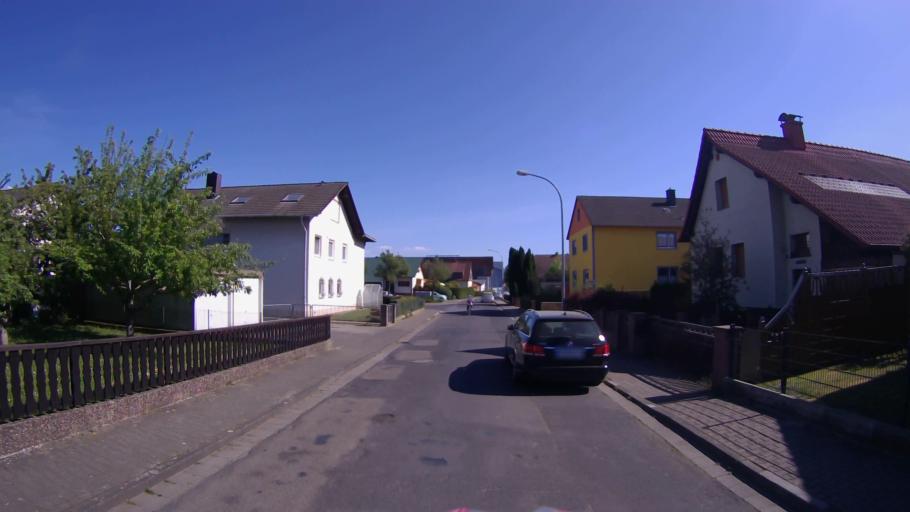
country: DE
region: Hesse
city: Hain-Grundau
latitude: 50.2003
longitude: 9.1161
